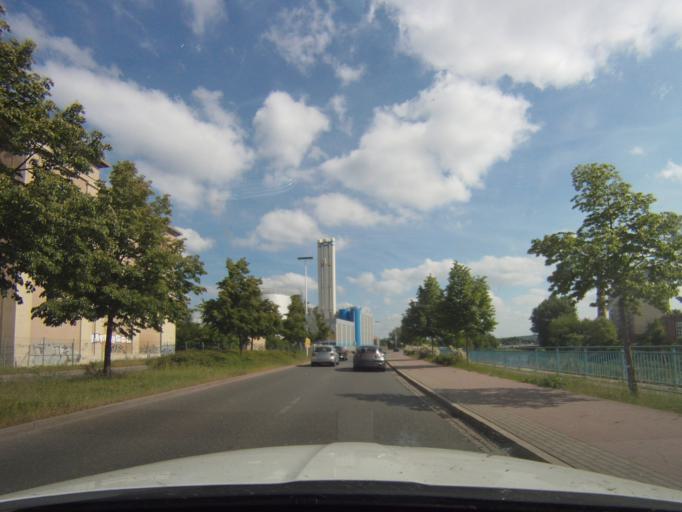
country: DE
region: Thuringia
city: Gera
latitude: 50.8664
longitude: 12.0788
